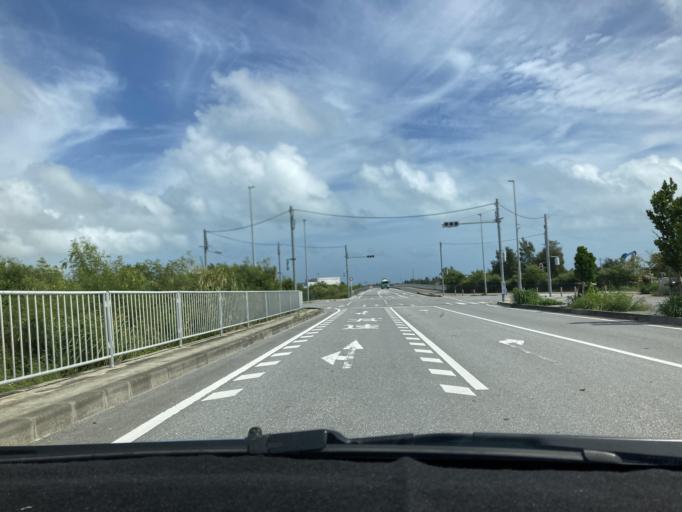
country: JP
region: Okinawa
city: Ginowan
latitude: 26.2129
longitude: 127.7684
